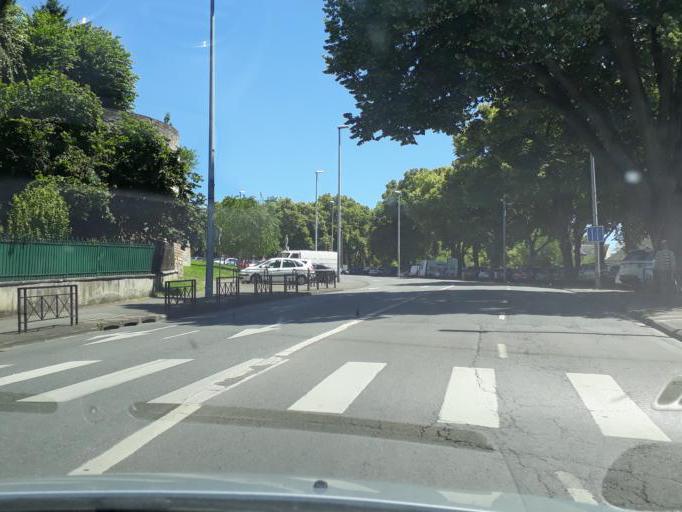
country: FR
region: Centre
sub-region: Departement du Cher
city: Bourges
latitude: 47.0795
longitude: 2.3958
